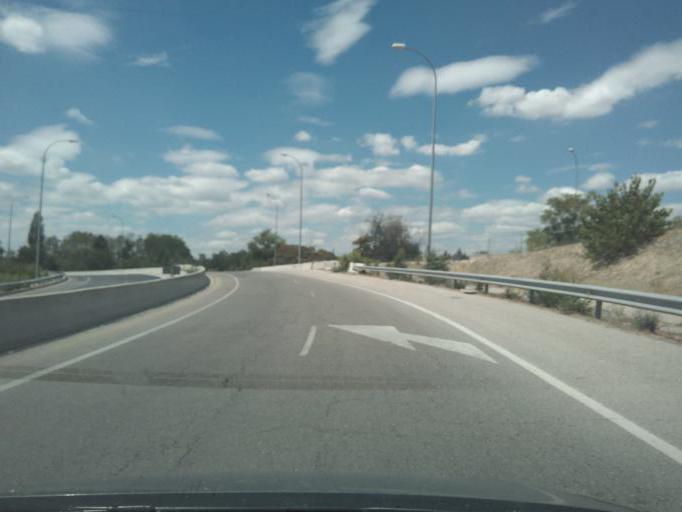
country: ES
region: Madrid
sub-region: Provincia de Madrid
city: San Sebastian de los Reyes
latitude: 40.5783
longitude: -3.5868
